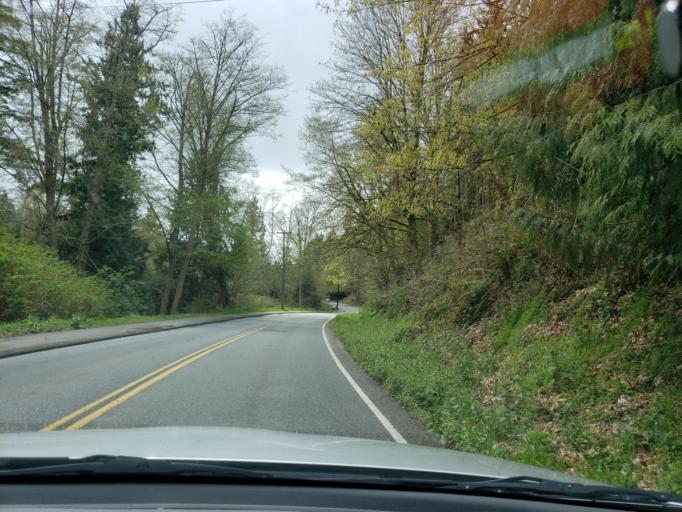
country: US
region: Washington
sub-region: Snohomish County
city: Meadowdale
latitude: 47.8346
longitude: -122.3391
